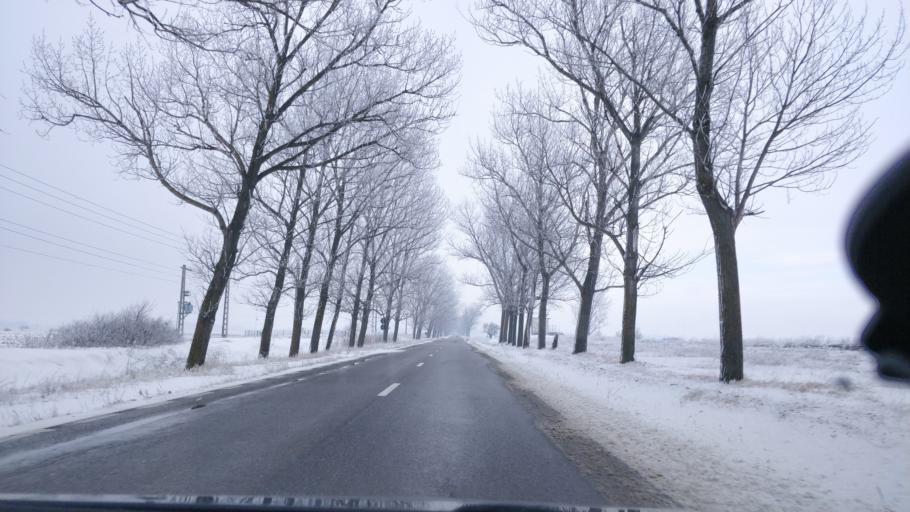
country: RO
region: Vrancea
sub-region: Comuna Vanatori
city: Jorasti
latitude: 45.6973
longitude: 27.2638
